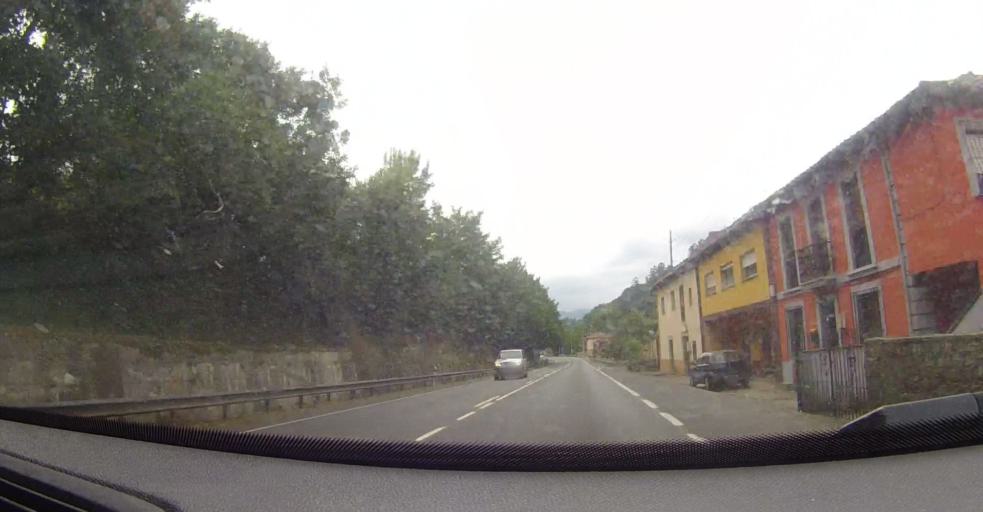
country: ES
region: Asturias
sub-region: Province of Asturias
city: Pilona
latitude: 43.3480
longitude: -5.3478
